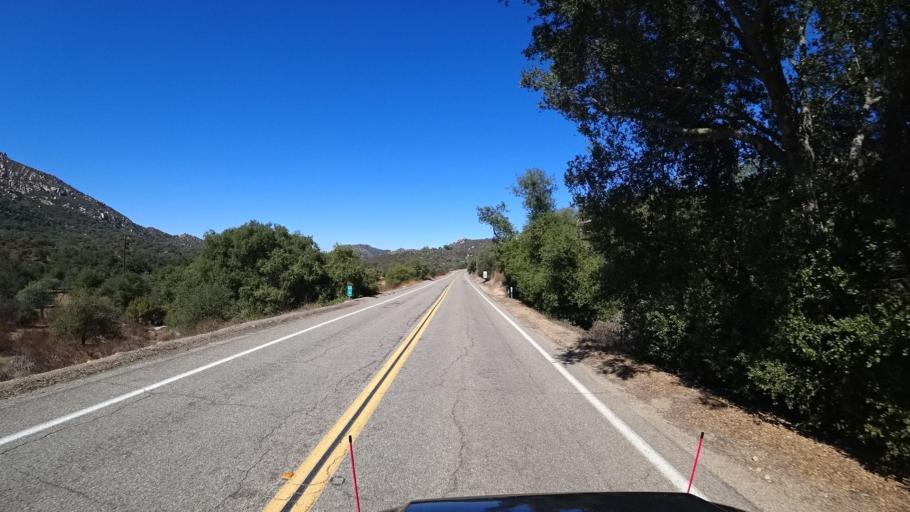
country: US
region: California
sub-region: San Diego County
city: Alpine
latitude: 32.7141
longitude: -116.7496
